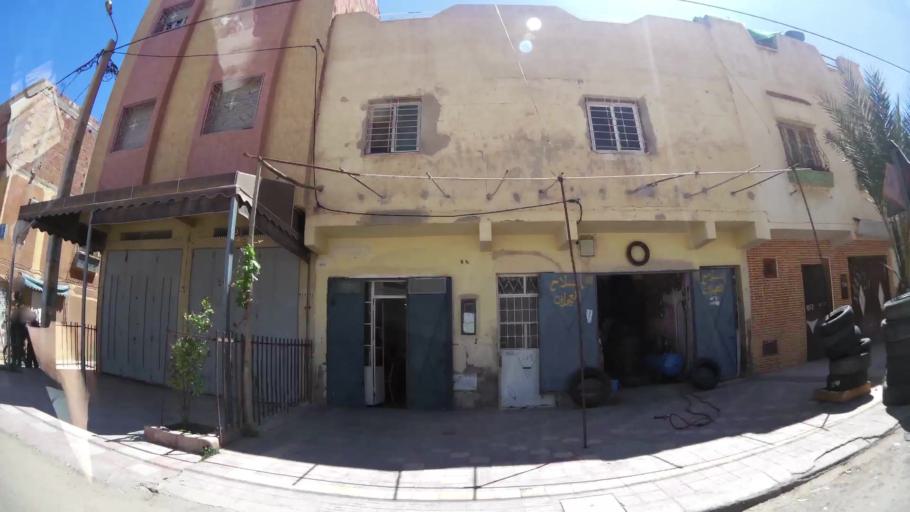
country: MA
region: Oriental
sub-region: Oujda-Angad
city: Oujda
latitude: 34.6622
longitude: -1.8812
